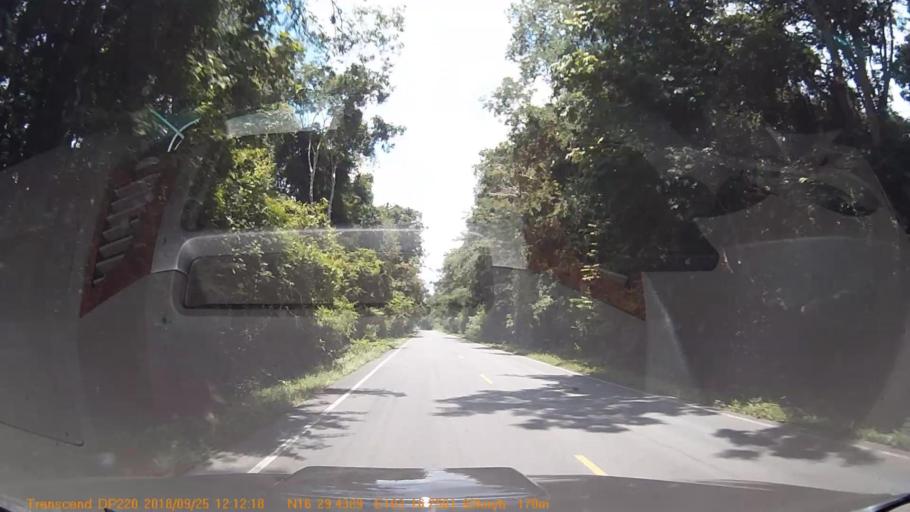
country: TH
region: Kalasin
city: Huai Mek
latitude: 16.4905
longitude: 103.2708
